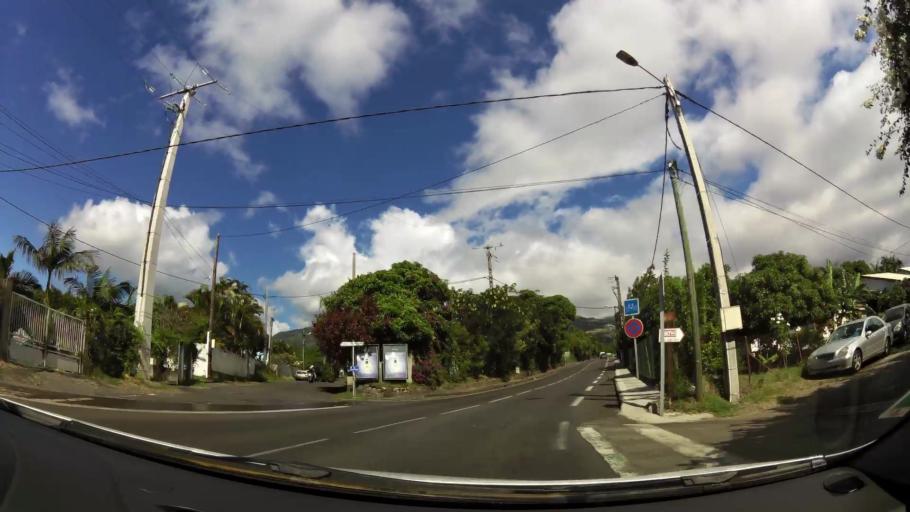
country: RE
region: Reunion
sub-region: Reunion
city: Sainte-Marie
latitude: -20.9128
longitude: 55.4980
